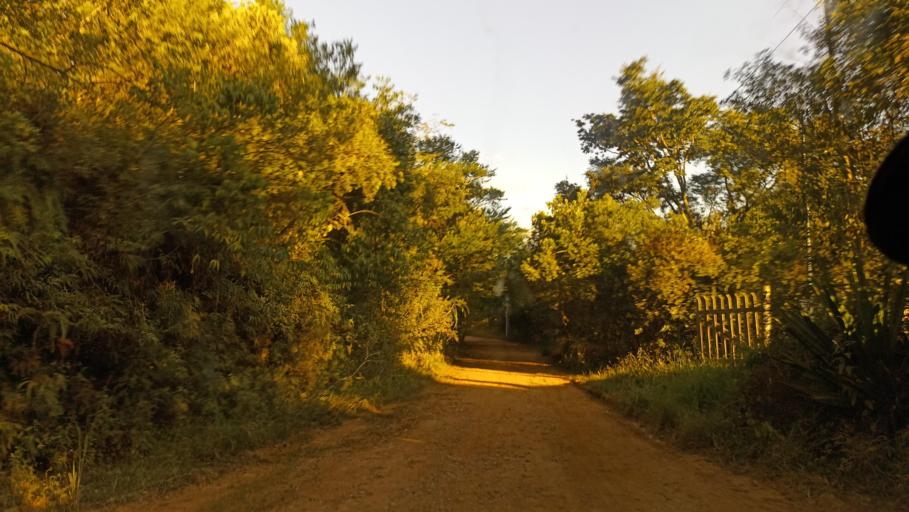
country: BR
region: Minas Gerais
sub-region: Sao Joao Del Rei
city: Sao Joao del Rei
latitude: -21.1820
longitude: -44.3533
